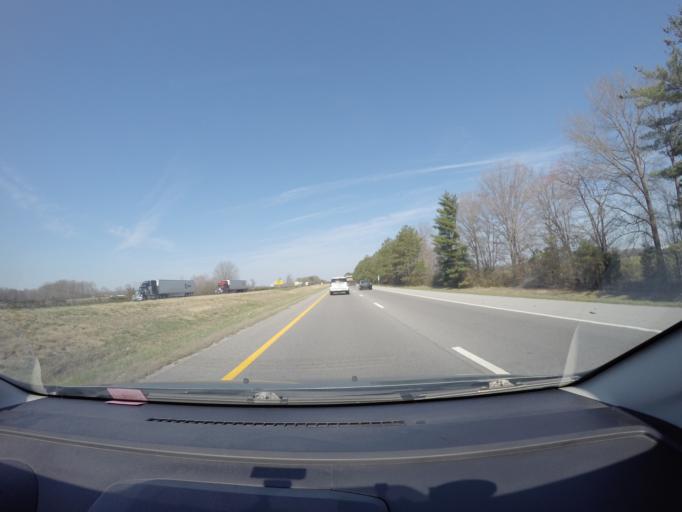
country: US
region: Tennessee
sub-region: Coffee County
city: New Union
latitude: 35.5160
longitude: -86.1191
